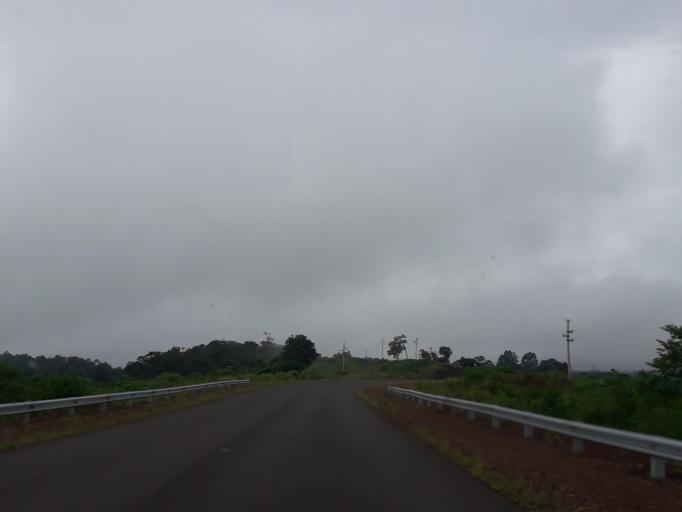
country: AR
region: Misiones
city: Bernardo de Irigoyen
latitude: -26.4143
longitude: -53.8235
